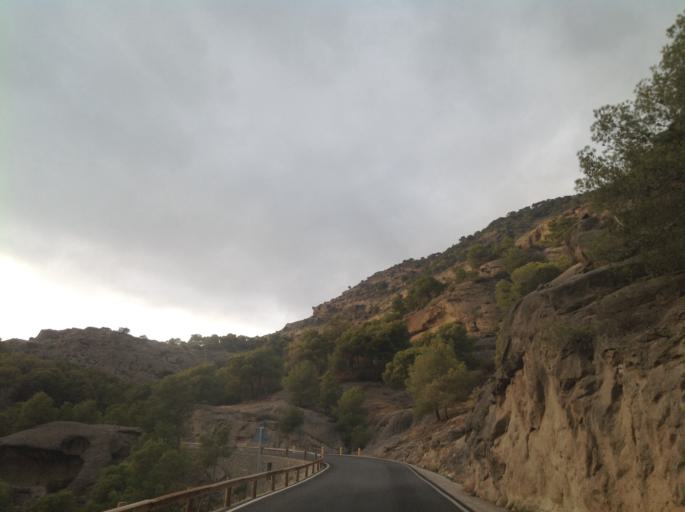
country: ES
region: Andalusia
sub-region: Provincia de Malaga
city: Ardales
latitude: 36.9125
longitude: -4.7925
